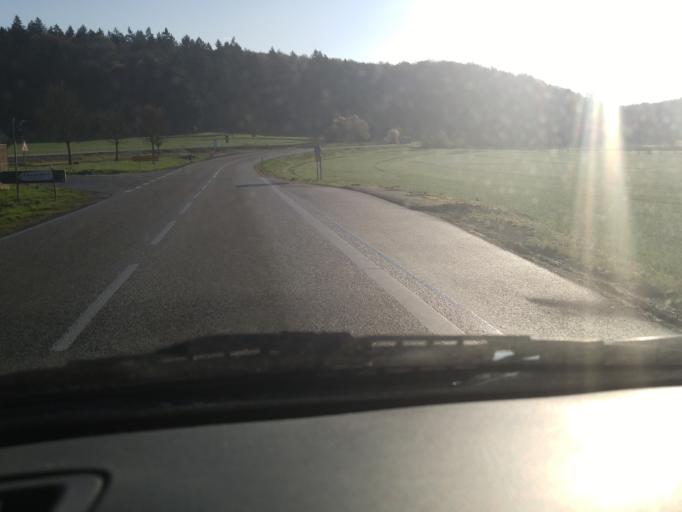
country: DE
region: Hesse
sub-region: Regierungsbezirk Darmstadt
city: Echzell
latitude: 50.4182
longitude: 8.9393
